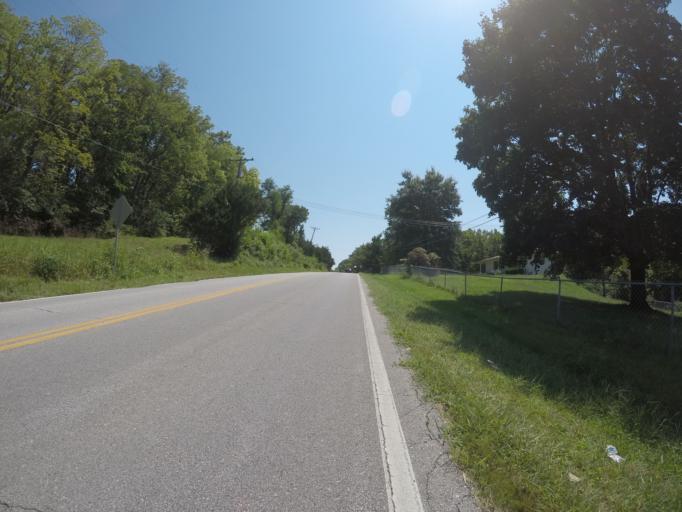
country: US
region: Missouri
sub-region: Platte County
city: Weston
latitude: 39.4086
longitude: -94.8839
